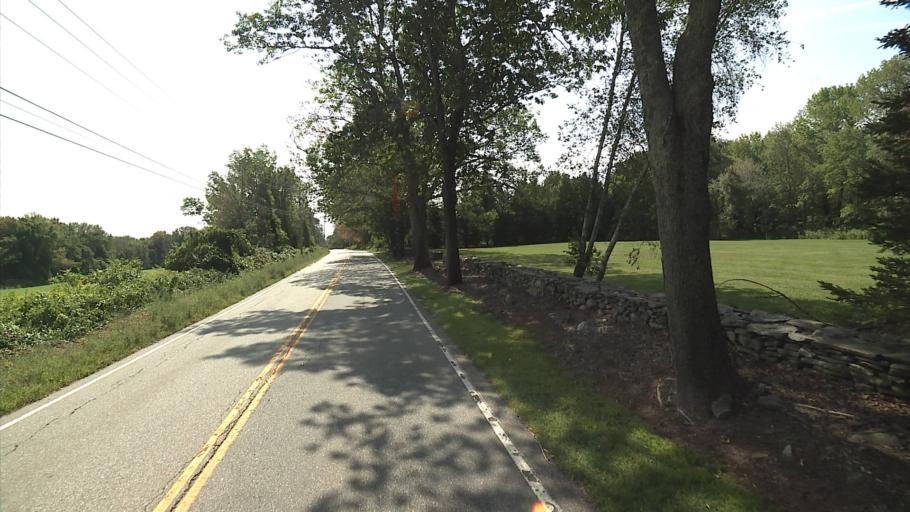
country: US
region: Connecticut
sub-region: Windham County
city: East Brooklyn
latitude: 41.8160
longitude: -71.9576
